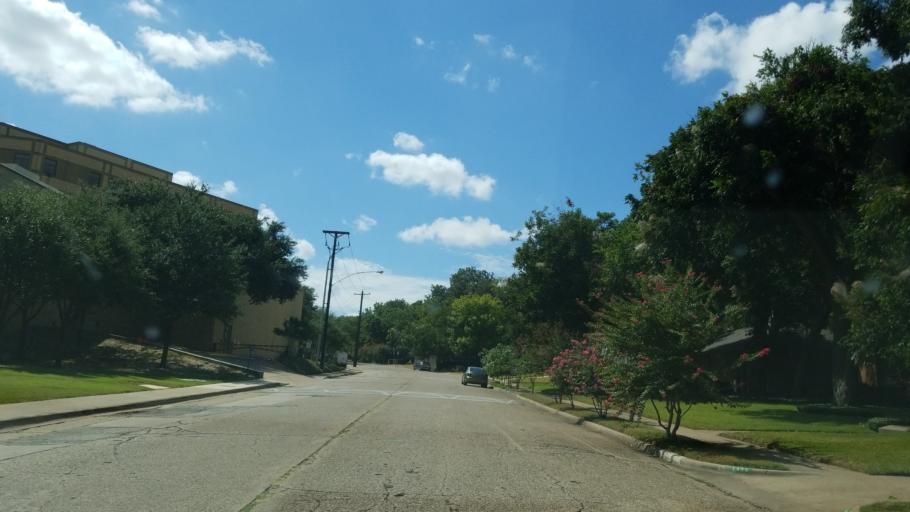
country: US
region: Texas
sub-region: Dallas County
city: Dallas
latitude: 32.7617
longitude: -96.8270
